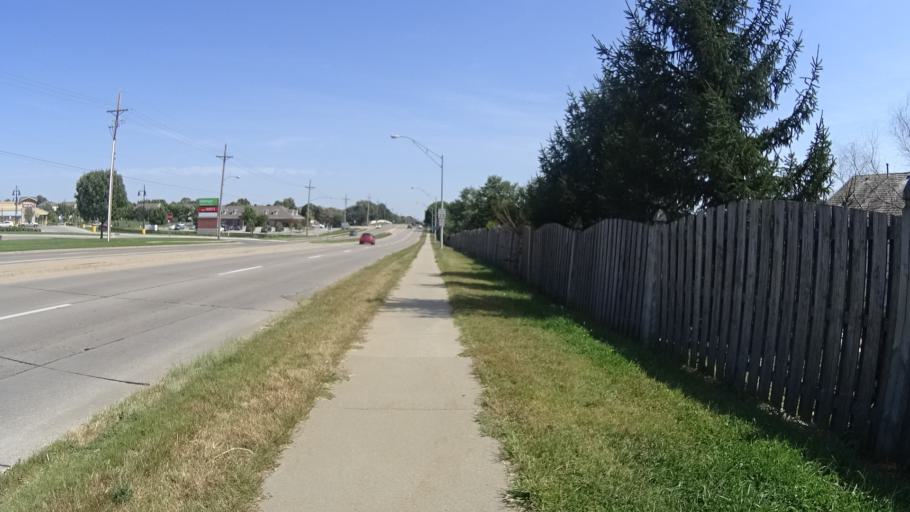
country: US
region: Nebraska
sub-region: Sarpy County
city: Papillion
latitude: 41.1761
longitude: -96.0616
